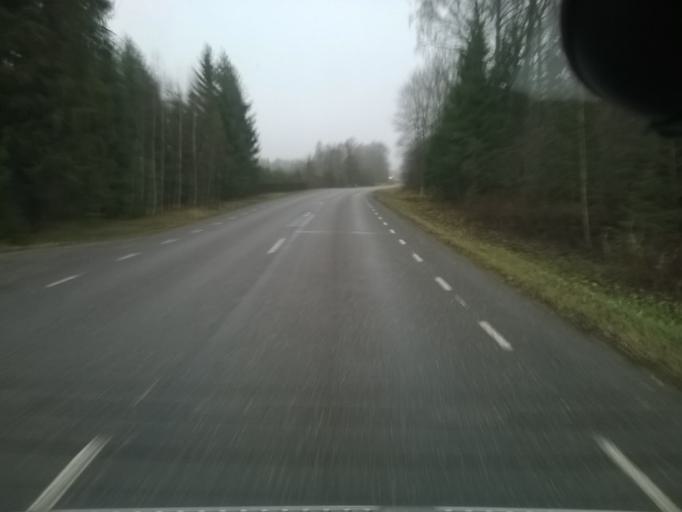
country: EE
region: Raplamaa
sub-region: Kohila vald
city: Kohila
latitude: 59.1544
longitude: 24.6254
